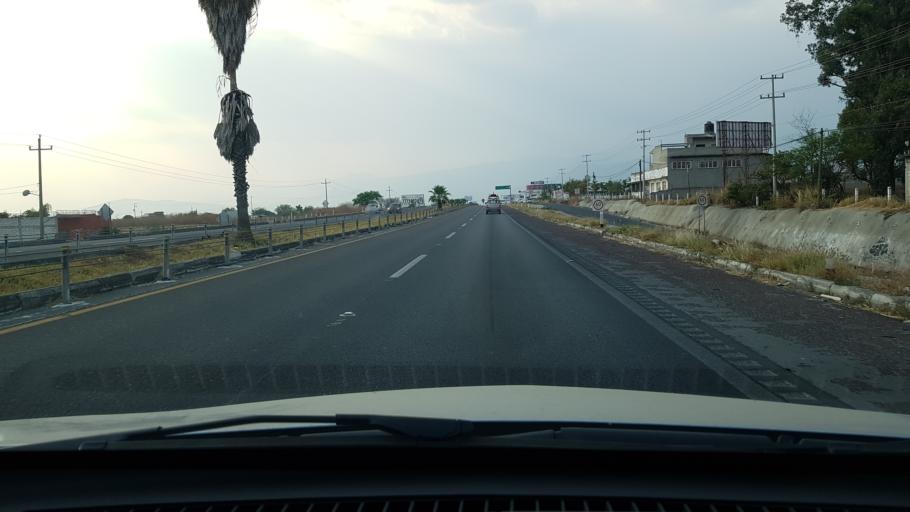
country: MX
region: Morelos
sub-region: Cuautla
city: Tierra Larga (Campo Nuevo)
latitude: 18.8605
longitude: -98.9454
